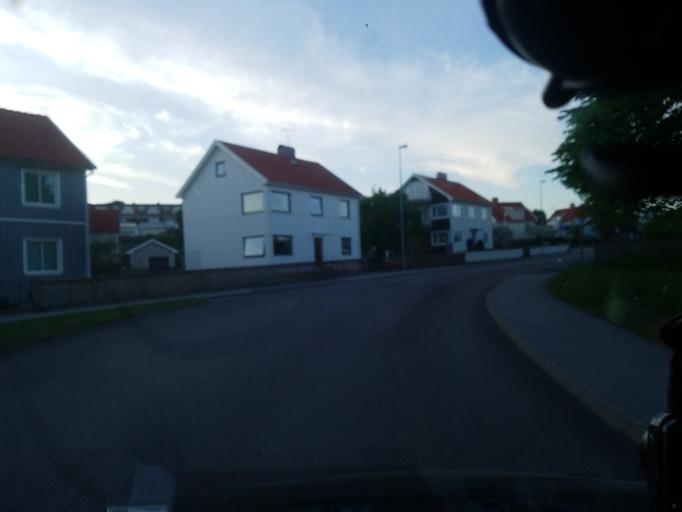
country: SE
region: Vaestra Goetaland
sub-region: Lysekils Kommun
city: Lysekil
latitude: 58.2787
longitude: 11.4548
